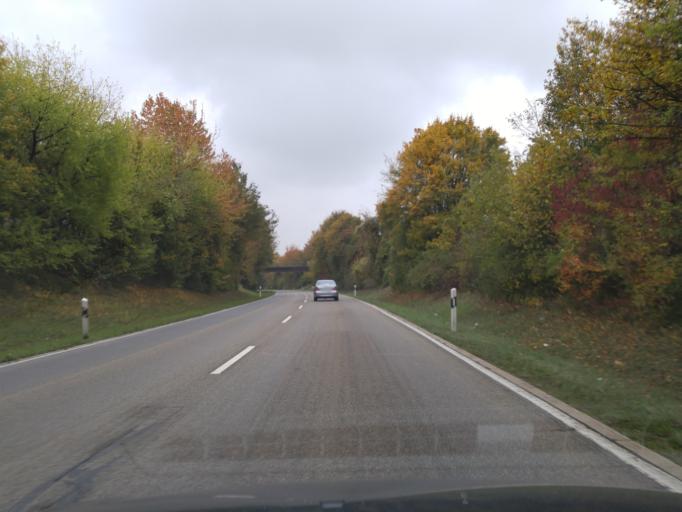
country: DE
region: Baden-Wuerttemberg
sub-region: Regierungsbezirk Stuttgart
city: Bad Rappenau
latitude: 49.2261
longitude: 9.0780
